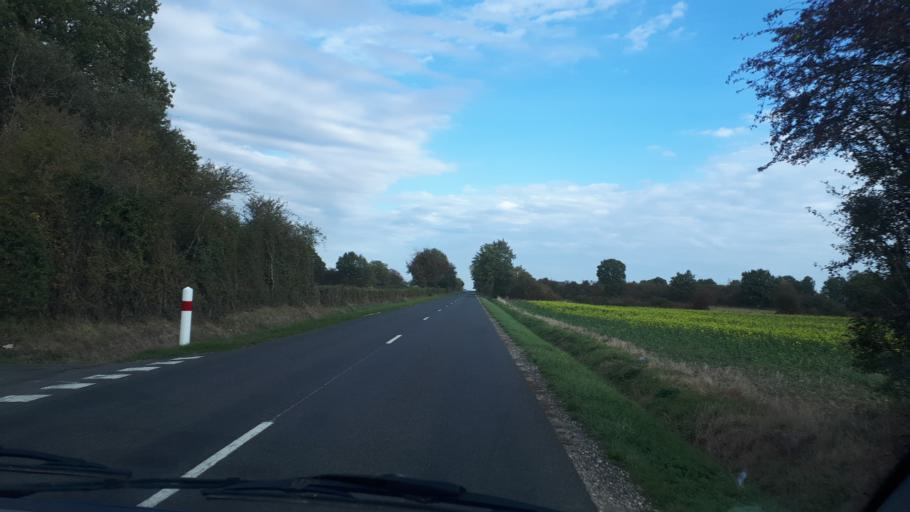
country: FR
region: Centre
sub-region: Departement du Loir-et-Cher
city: Mondoubleau
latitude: 47.9426
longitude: 0.9328
